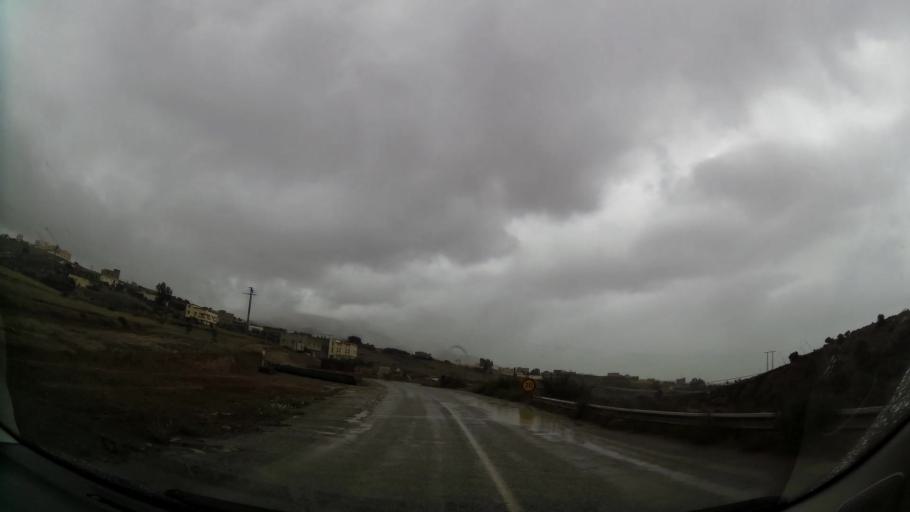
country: MA
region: Oriental
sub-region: Nador
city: Midar
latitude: 34.8906
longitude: -3.7463
